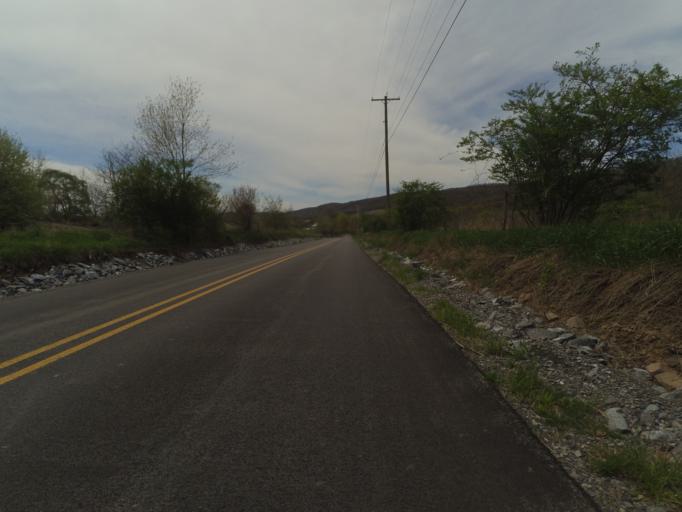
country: US
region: Pennsylvania
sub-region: Blair County
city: Tyrone
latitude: 40.6932
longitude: -78.1853
